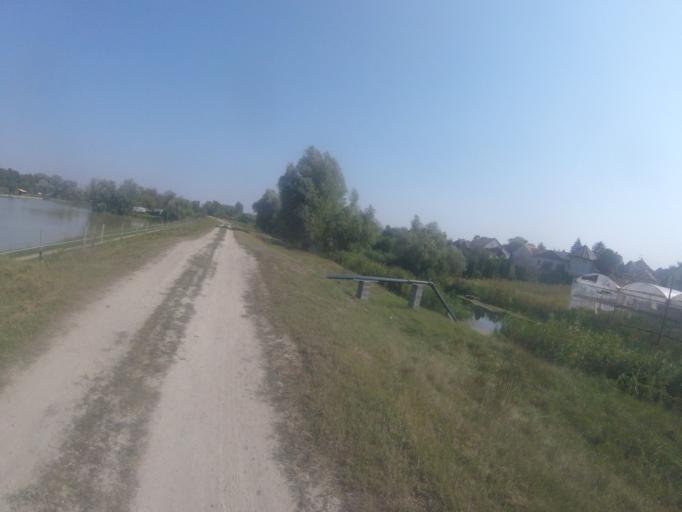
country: HU
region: Bacs-Kiskun
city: Baja
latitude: 46.2070
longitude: 18.9567
